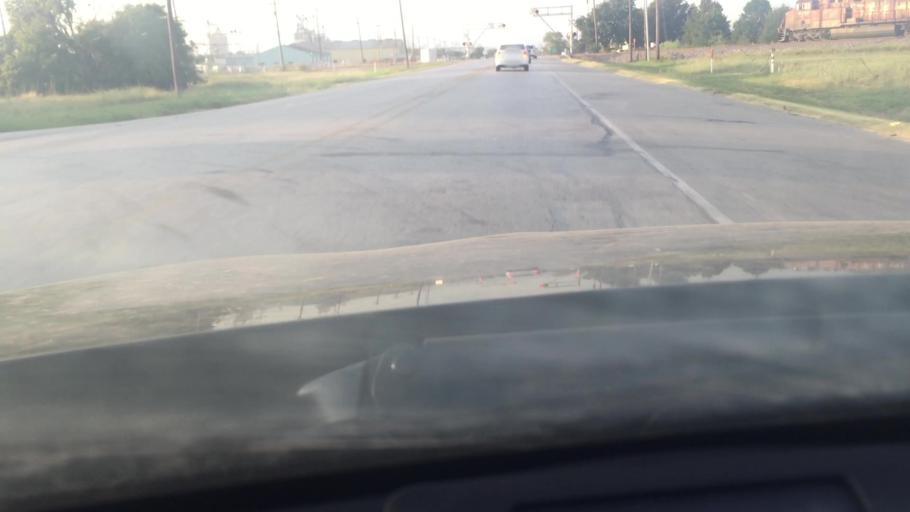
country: US
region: Texas
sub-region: Tarrant County
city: Blue Mound
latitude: 32.8387
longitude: -97.3431
